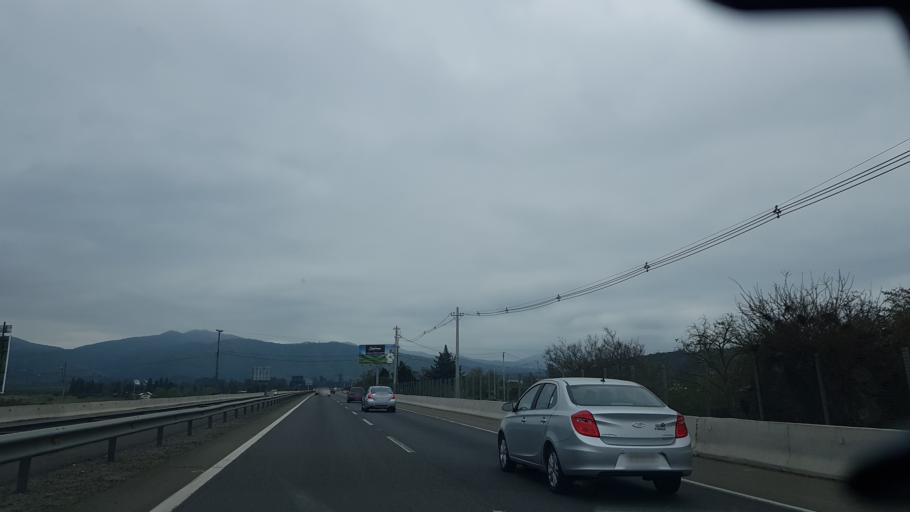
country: CL
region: Santiago Metropolitan
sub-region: Provincia de Melipilla
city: Melipilla
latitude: -33.4097
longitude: -71.1403
